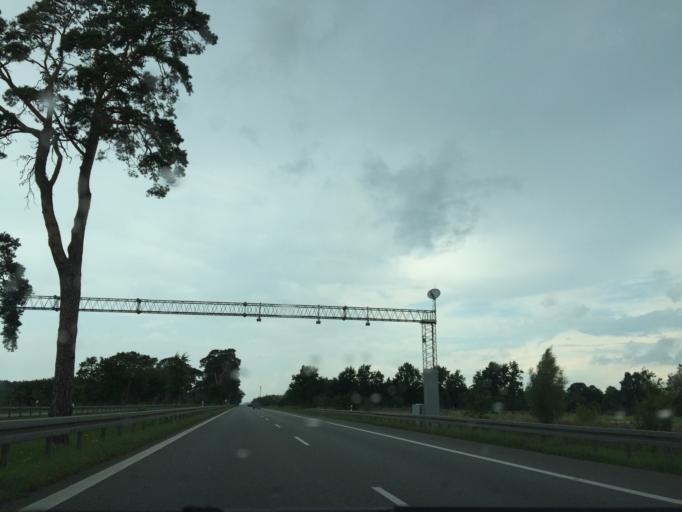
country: PL
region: Masovian Voivodeship
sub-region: Powiat bialobrzeski
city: Stara Blotnica
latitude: 51.5899
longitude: 20.9960
